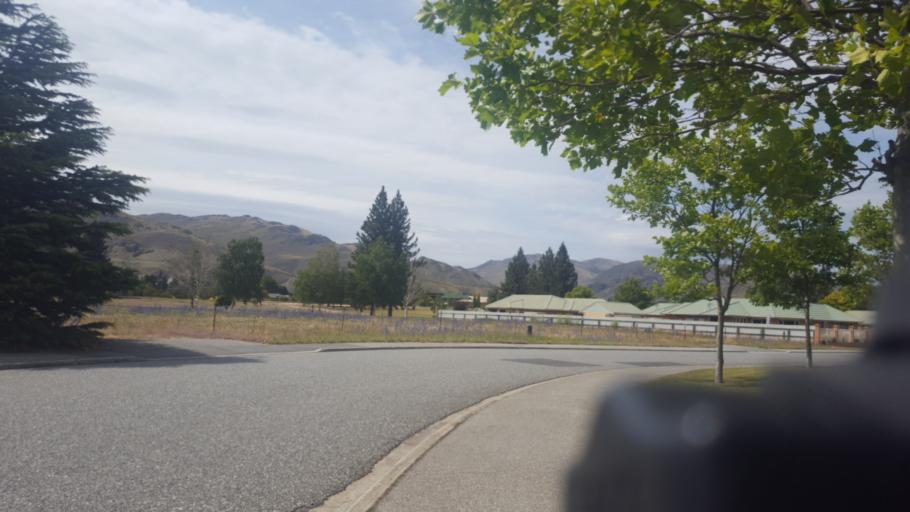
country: NZ
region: Otago
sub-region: Queenstown-Lakes District
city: Wanaka
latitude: -45.0382
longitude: 169.1997
